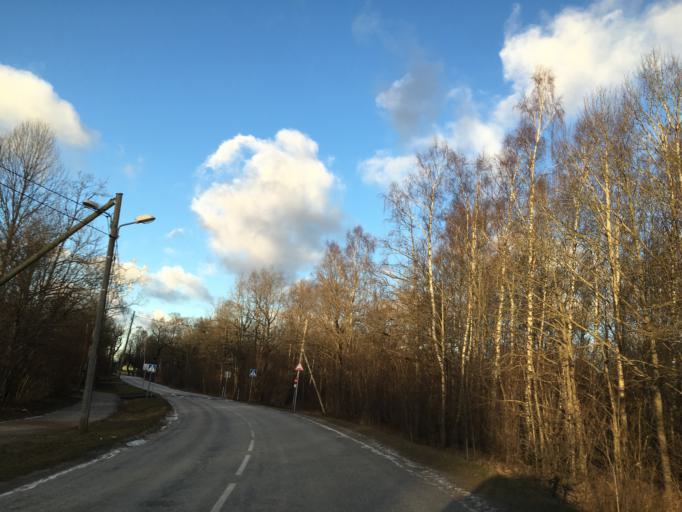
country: EE
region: Harju
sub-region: Saue linn
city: Saue
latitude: 59.3172
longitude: 24.5585
